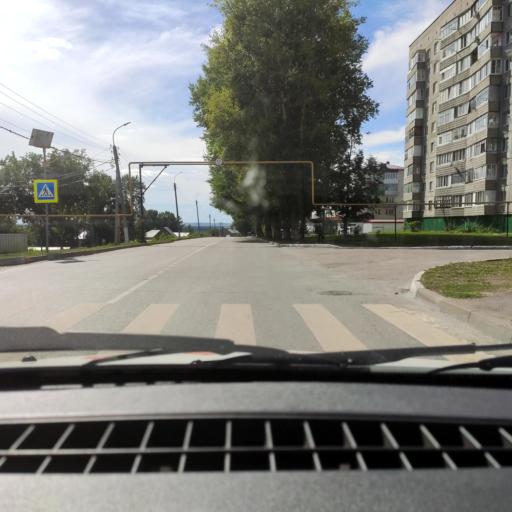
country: RU
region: Bashkortostan
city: Blagoveshchensk
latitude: 55.0449
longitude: 55.9549
